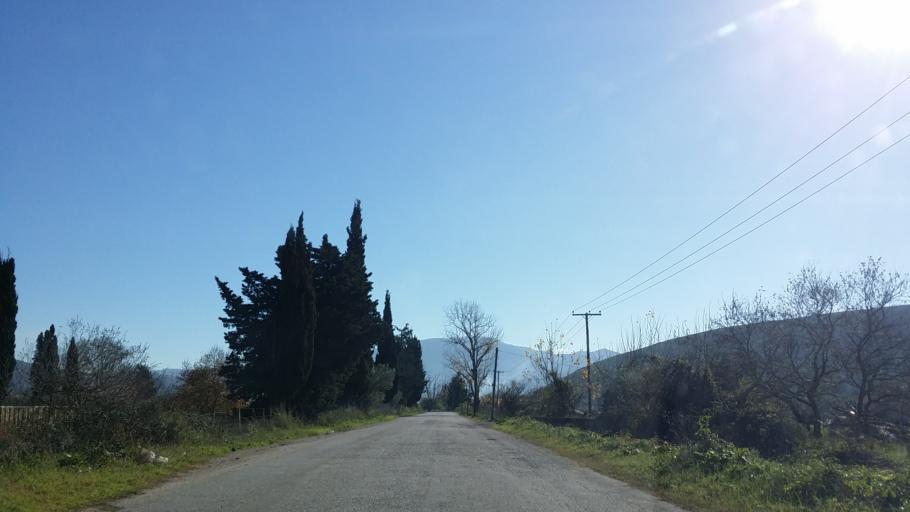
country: GR
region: West Greece
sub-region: Nomos Aitolias kai Akarnanias
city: Vonitsa
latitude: 38.9131
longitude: 20.8835
